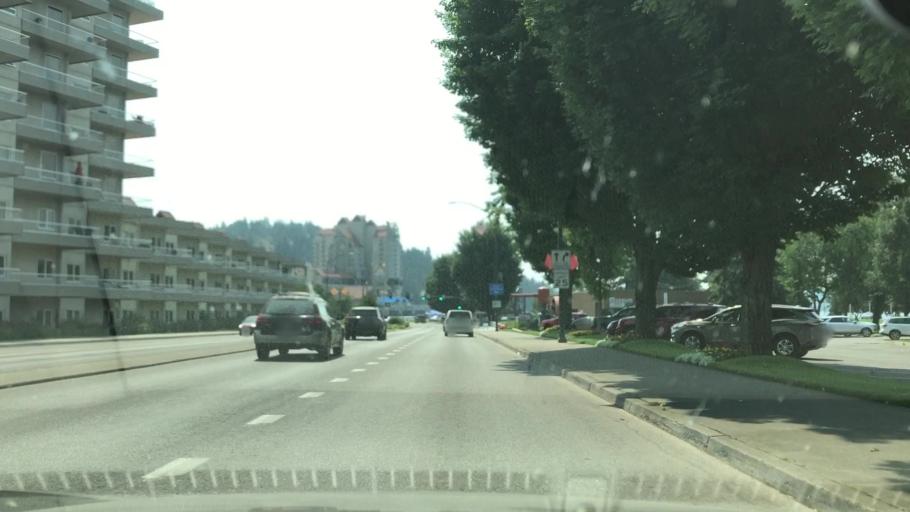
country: US
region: Idaho
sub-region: Kootenai County
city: Coeur d'Alene
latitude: 47.6756
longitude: -116.7875
